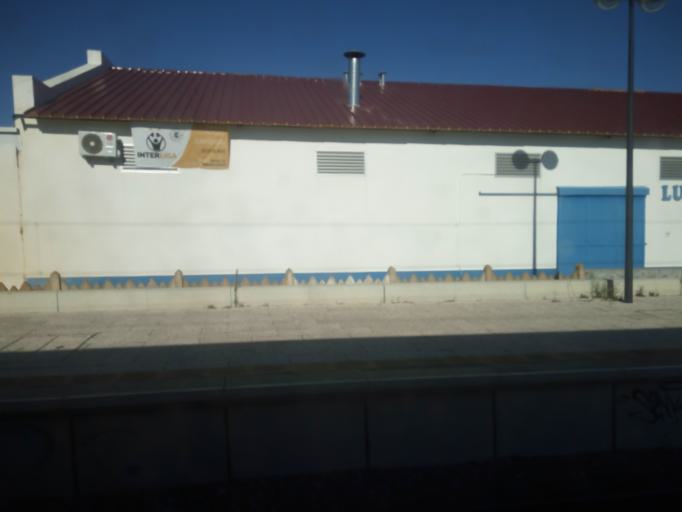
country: PT
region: Faro
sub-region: Albufeira
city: Ferreiras
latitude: 37.1289
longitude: -8.2337
